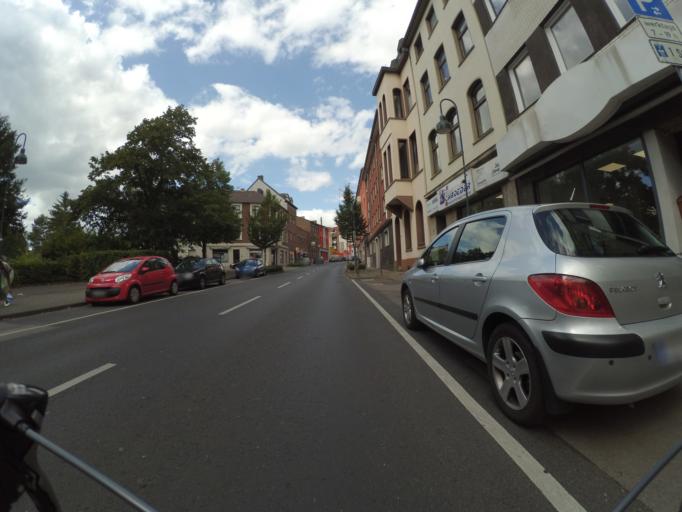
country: DE
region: North Rhine-Westphalia
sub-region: Regierungsbezirk Koln
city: Wurselen
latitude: 50.7965
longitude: 6.1257
